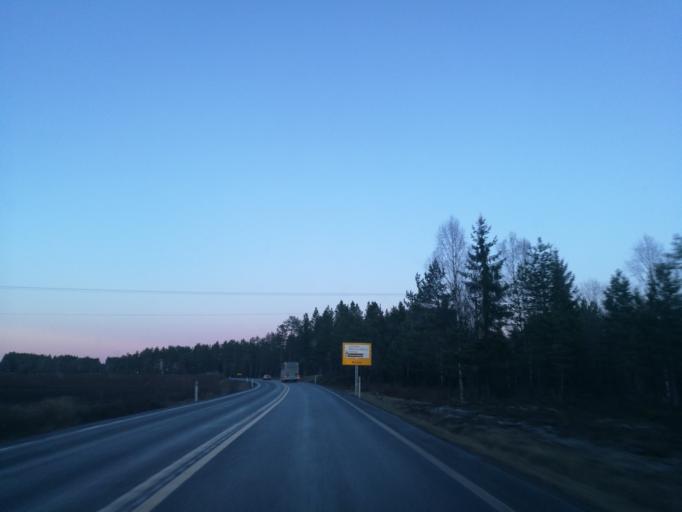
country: NO
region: Hedmark
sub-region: Eidskog
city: Skotterud
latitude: 60.0263
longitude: 12.1184
